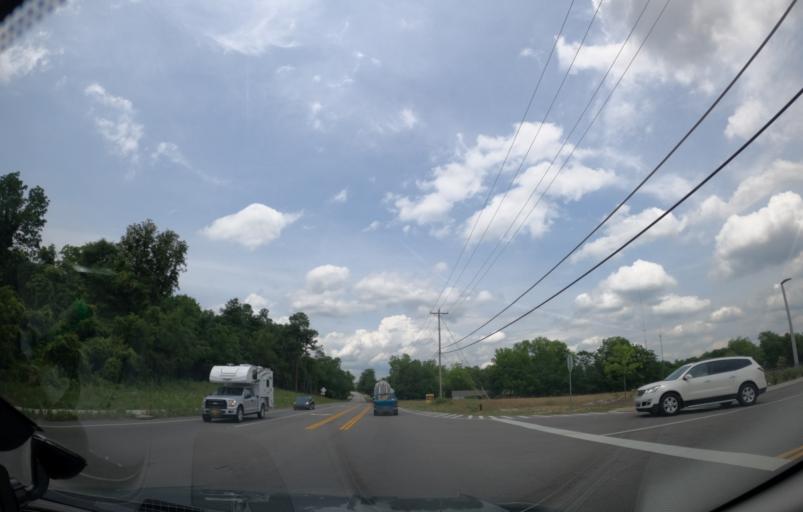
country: US
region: South Carolina
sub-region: Aiken County
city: Aiken
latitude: 33.5813
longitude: -81.7197
